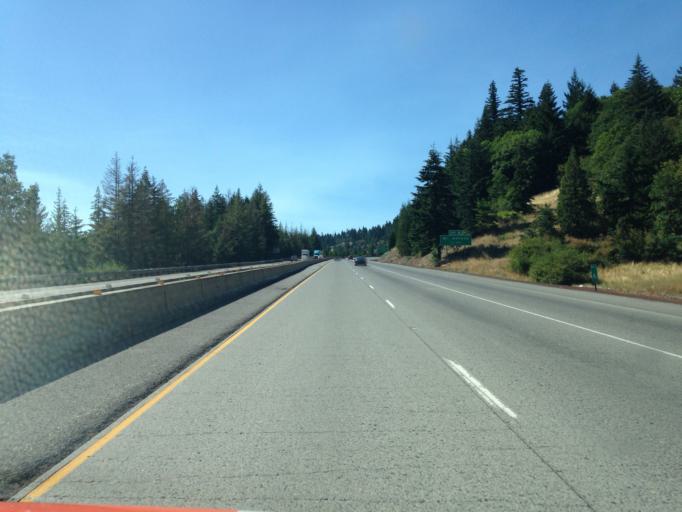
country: US
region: Oregon
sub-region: Jackson County
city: Ashland
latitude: 42.0813
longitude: -122.5995
